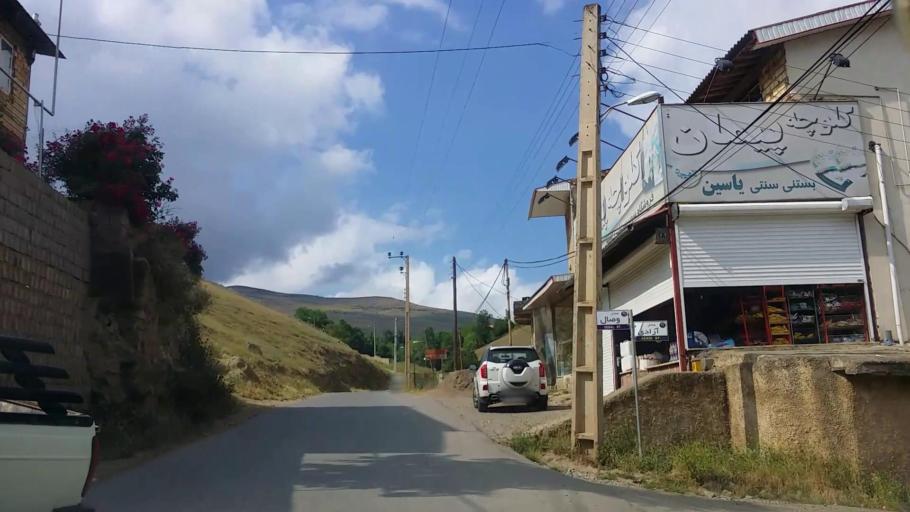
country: IR
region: Mazandaran
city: Chalus
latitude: 36.5156
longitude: 51.2592
